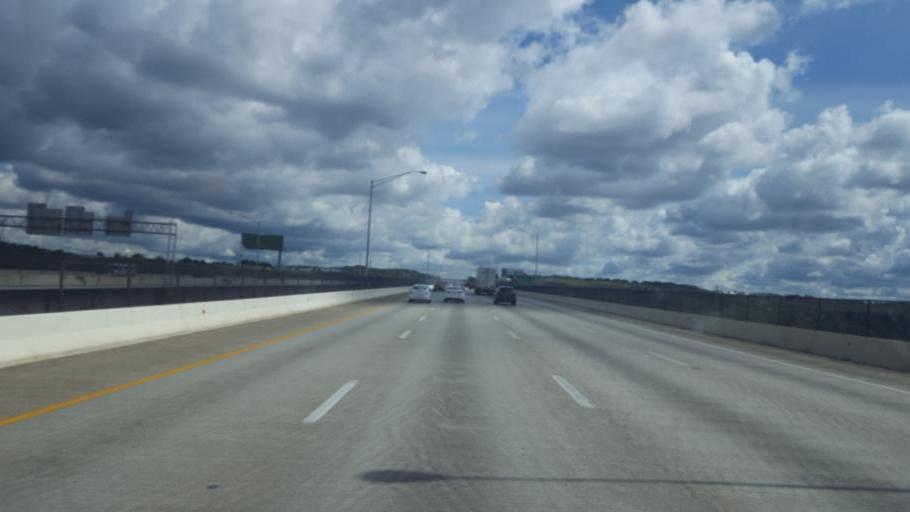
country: US
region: Ohio
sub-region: Cuyahoga County
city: Garfield Heights
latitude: 41.4082
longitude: -81.6340
